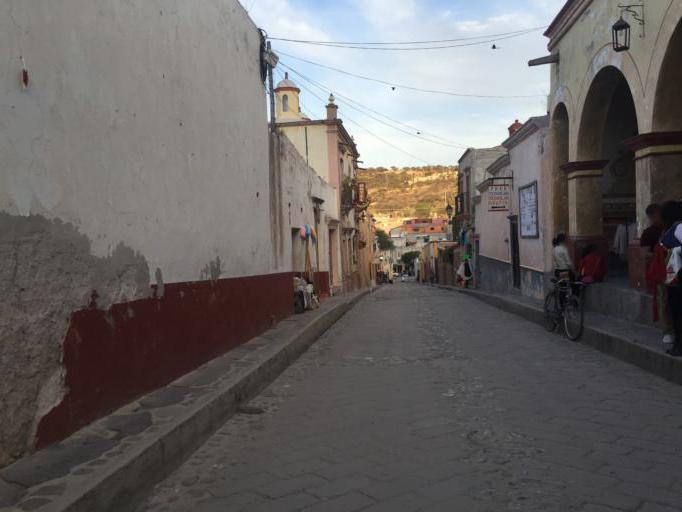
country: MX
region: Queretaro
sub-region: Ezequiel Montes
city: San Jose del Jagueey
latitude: 20.7398
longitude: -99.9411
